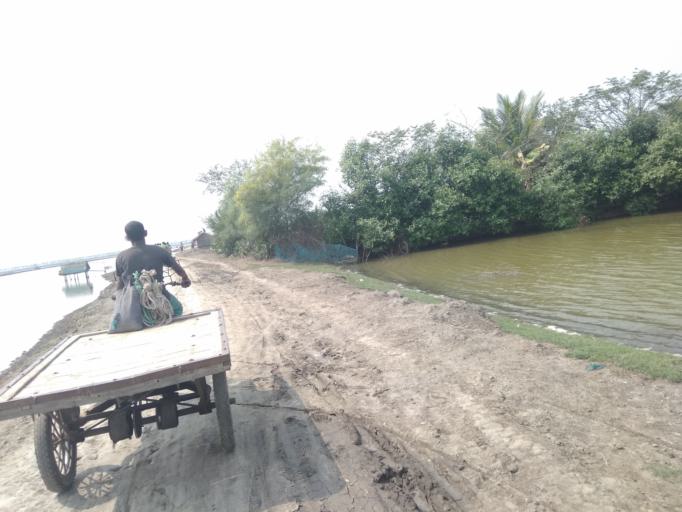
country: IN
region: West Bengal
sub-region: North 24 Parganas
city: Taki
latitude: 22.3441
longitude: 89.2318
